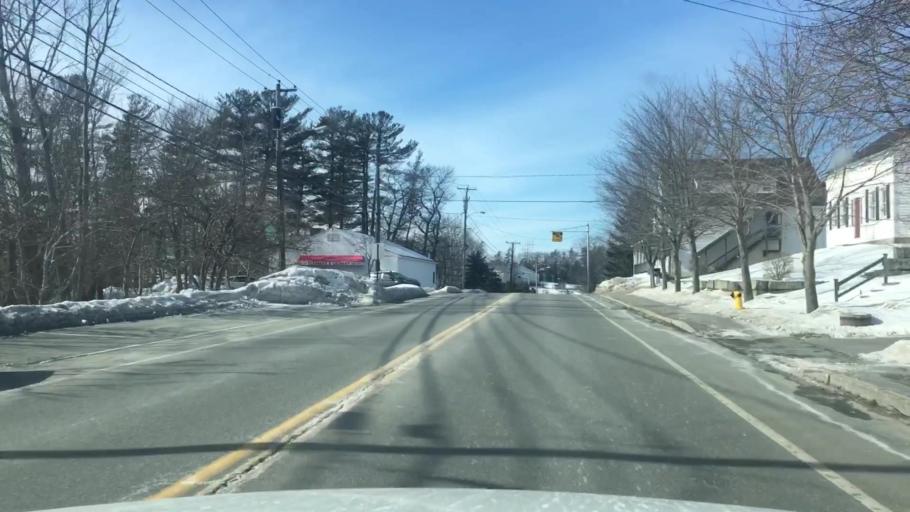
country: US
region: Maine
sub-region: Hancock County
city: Bucksport
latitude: 44.5752
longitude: -68.8013
